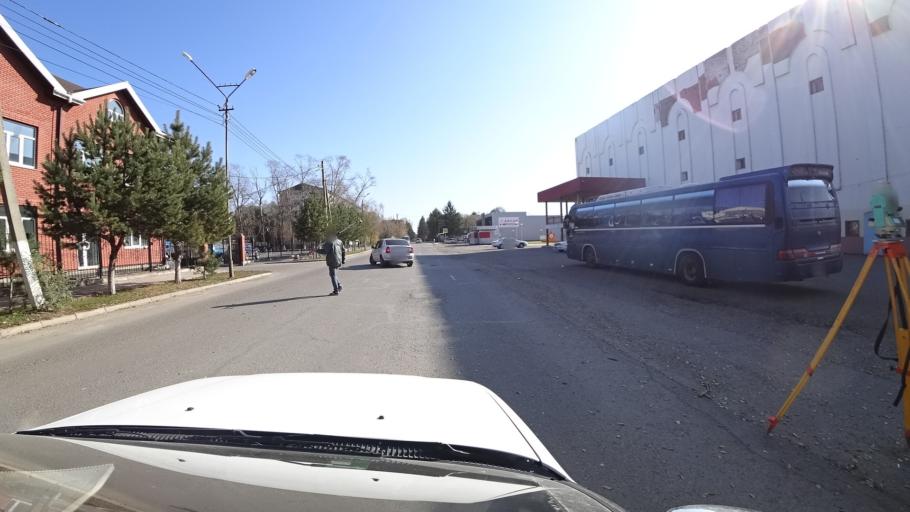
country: RU
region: Primorskiy
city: Dal'nerechensk
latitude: 45.9340
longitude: 133.7288
